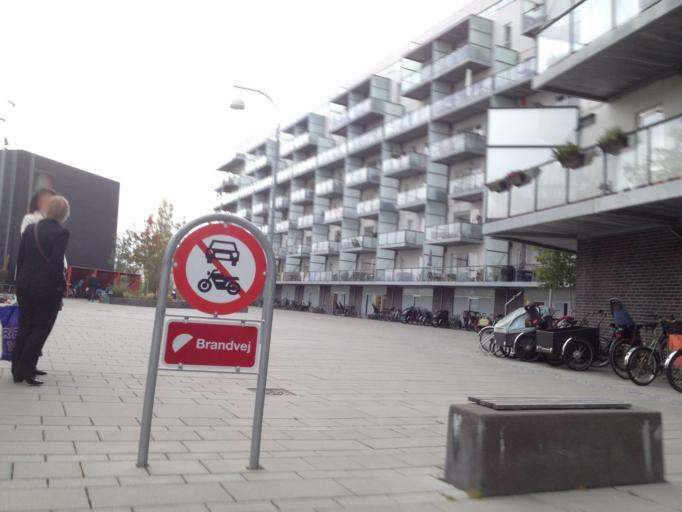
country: DK
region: Capital Region
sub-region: Kobenhavn
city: Christianshavn
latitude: 55.6858
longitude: 12.6153
